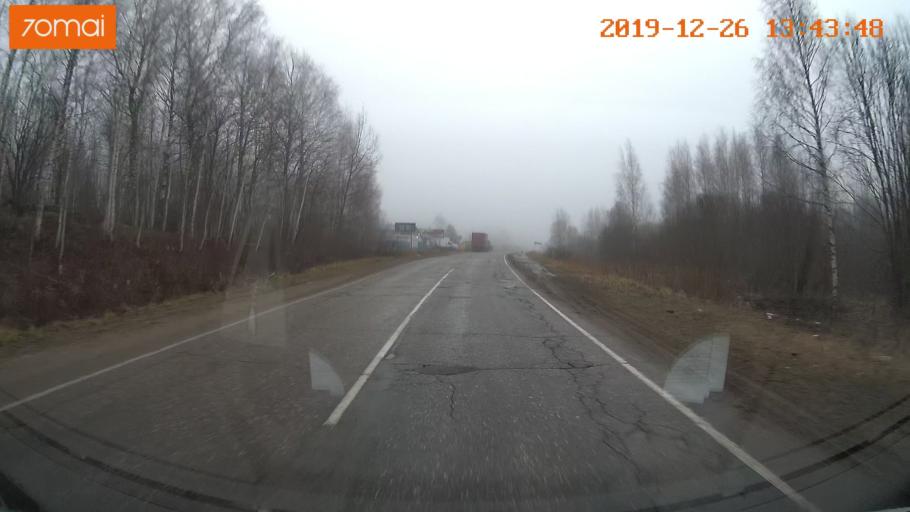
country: RU
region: Vologda
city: Sheksna
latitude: 58.7069
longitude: 38.4977
